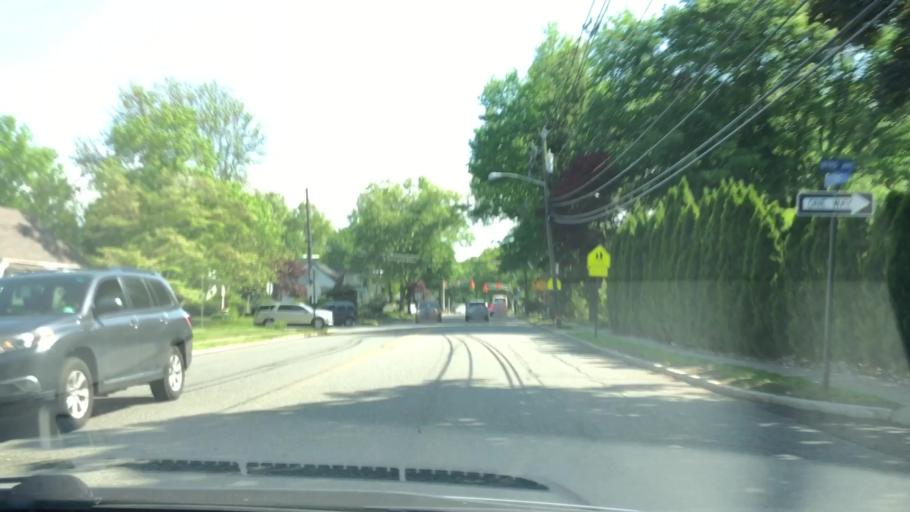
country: US
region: New Jersey
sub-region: Essex County
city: Brookdale
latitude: 40.8302
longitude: -74.1737
